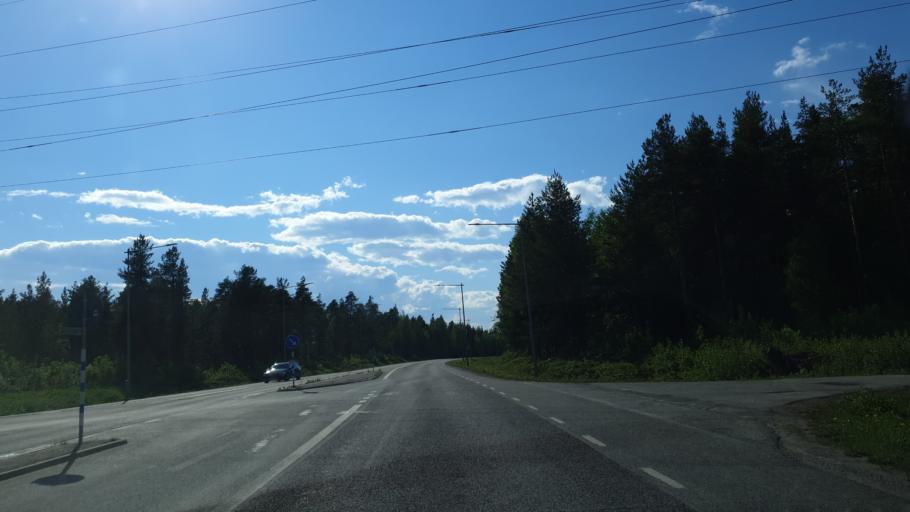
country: SE
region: Norrbotten
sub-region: Pitea Kommun
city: Pitea
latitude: 65.3308
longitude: 21.4568
